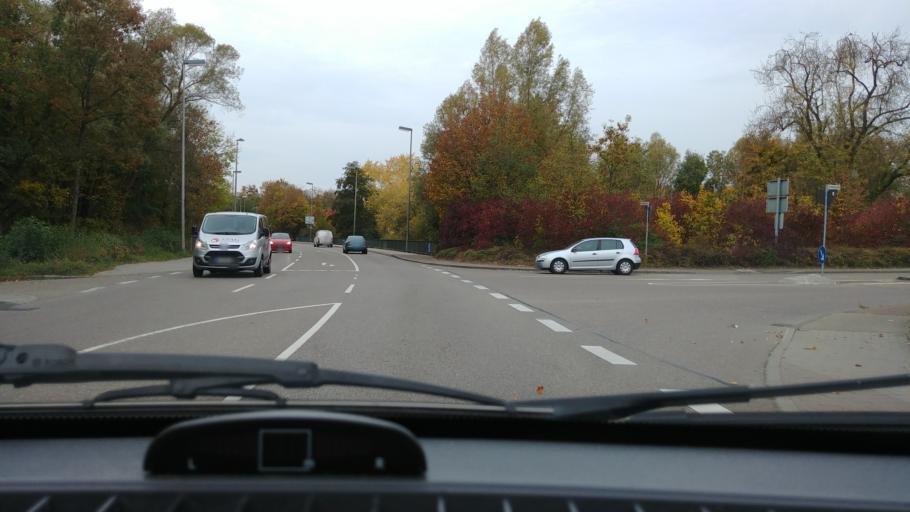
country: DE
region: Baden-Wuerttemberg
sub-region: Regierungsbezirk Stuttgart
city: Crailsheim
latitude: 49.1342
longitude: 10.0694
